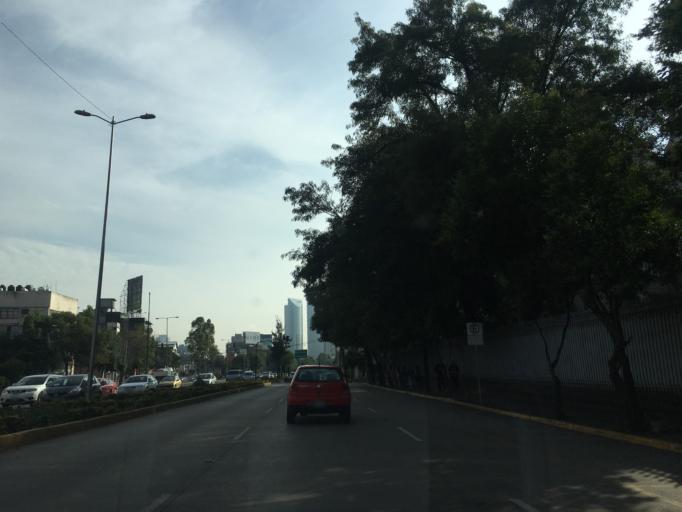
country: MX
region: Mexico City
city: Polanco
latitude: 19.4096
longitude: -99.1832
